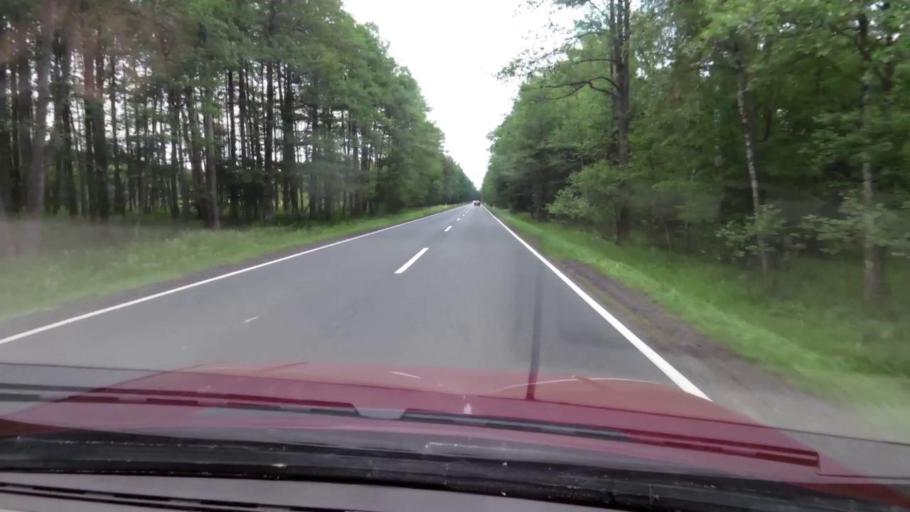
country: PL
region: Pomeranian Voivodeship
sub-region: Powiat bytowski
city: Trzebielino
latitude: 54.2245
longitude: 17.0874
